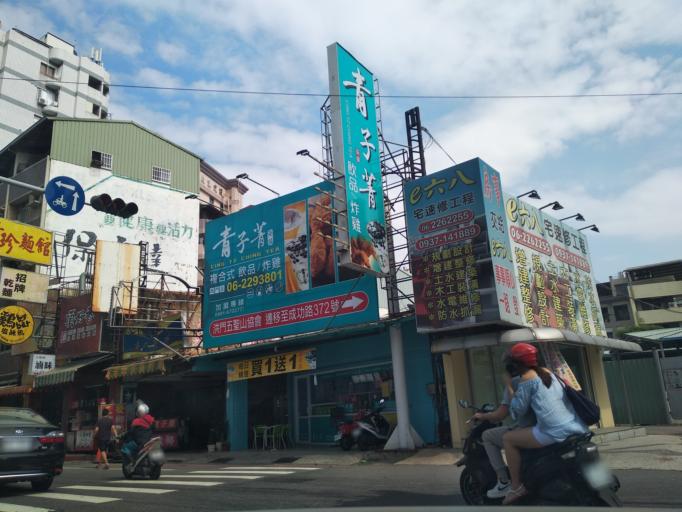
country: TW
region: Taiwan
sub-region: Tainan
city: Tainan
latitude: 23.0039
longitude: 120.2043
